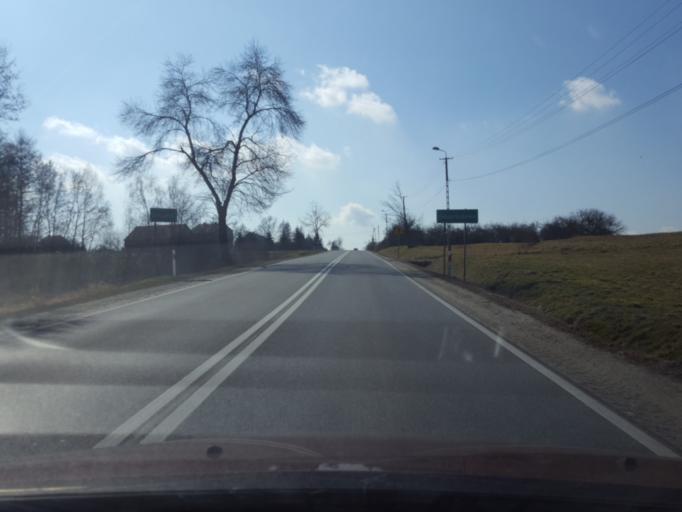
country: PL
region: Lesser Poland Voivodeship
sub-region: Powiat brzeski
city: Gnojnik
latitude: 49.8751
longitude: 20.6173
